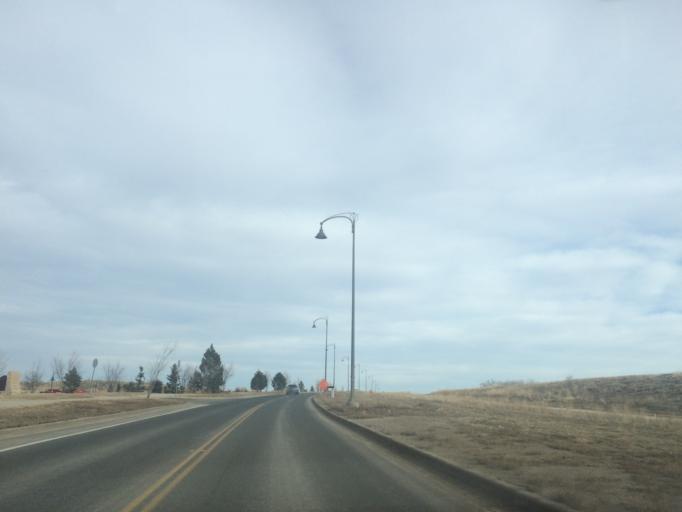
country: US
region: Colorado
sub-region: Boulder County
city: Lafayette
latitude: 39.9801
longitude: -105.0272
